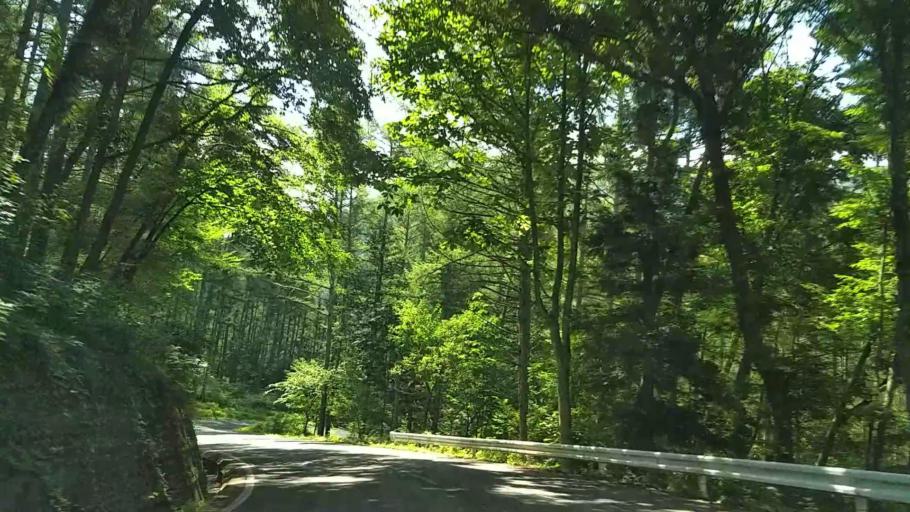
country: JP
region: Nagano
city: Matsumoto
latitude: 36.1970
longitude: 138.0667
